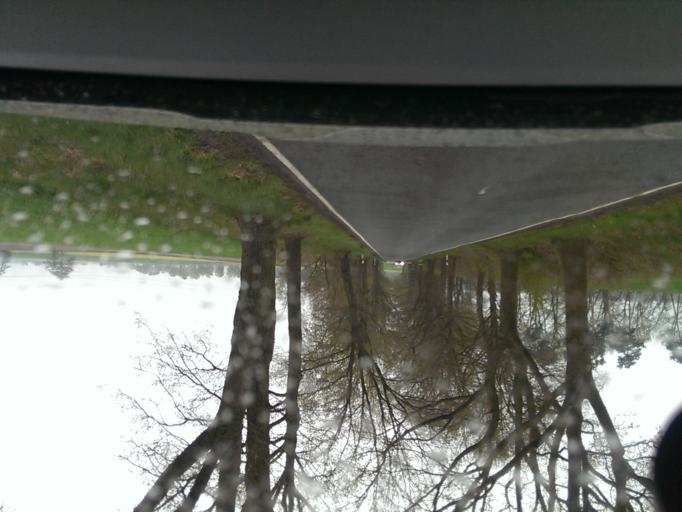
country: DE
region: Lower Saxony
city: Steimbke
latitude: 52.6052
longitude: 9.4704
